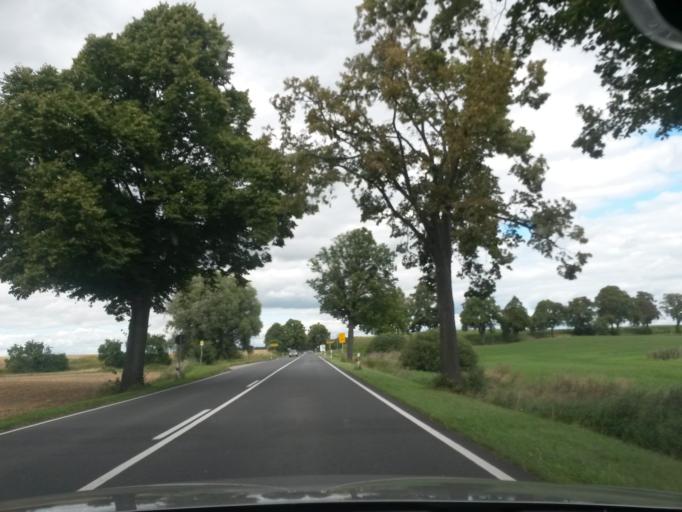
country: DE
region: Brandenburg
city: Angermunde
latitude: 52.9765
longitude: 13.9702
